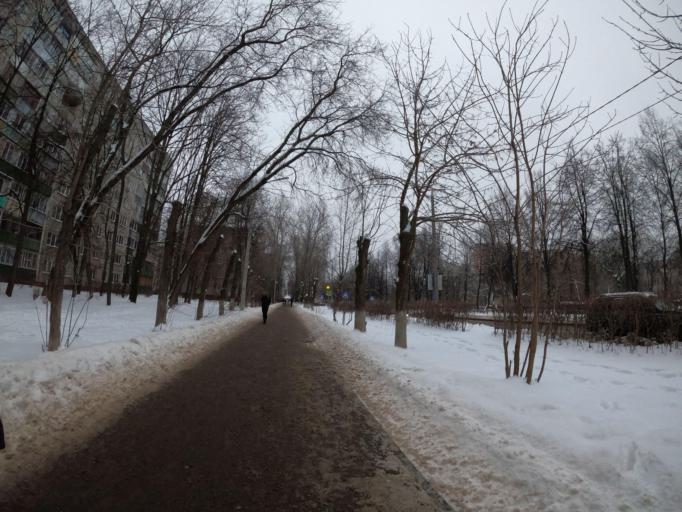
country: RU
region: Moskovskaya
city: Dubrovitsy
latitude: 55.4288
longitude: 37.4985
